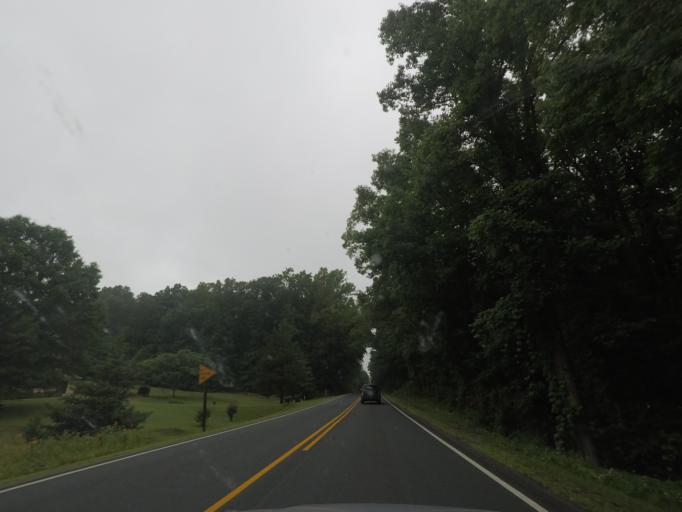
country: US
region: Virginia
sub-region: Charlotte County
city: Charlotte Court House
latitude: 37.0783
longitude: -78.4764
